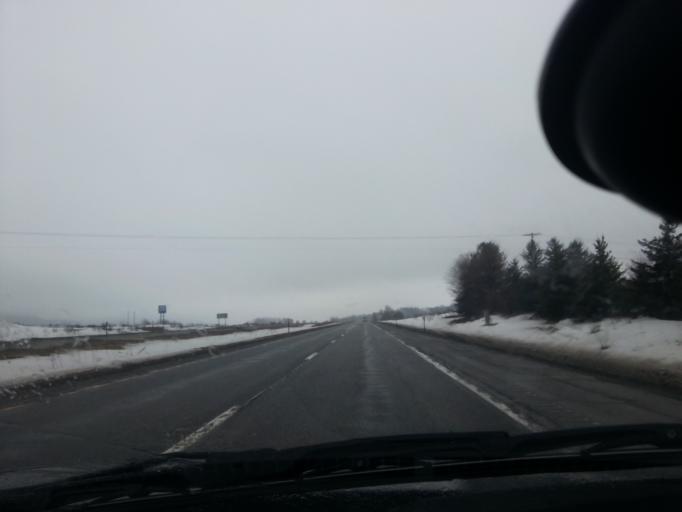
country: US
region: New York
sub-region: Cortland County
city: Homer
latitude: 42.7911
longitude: -76.1250
